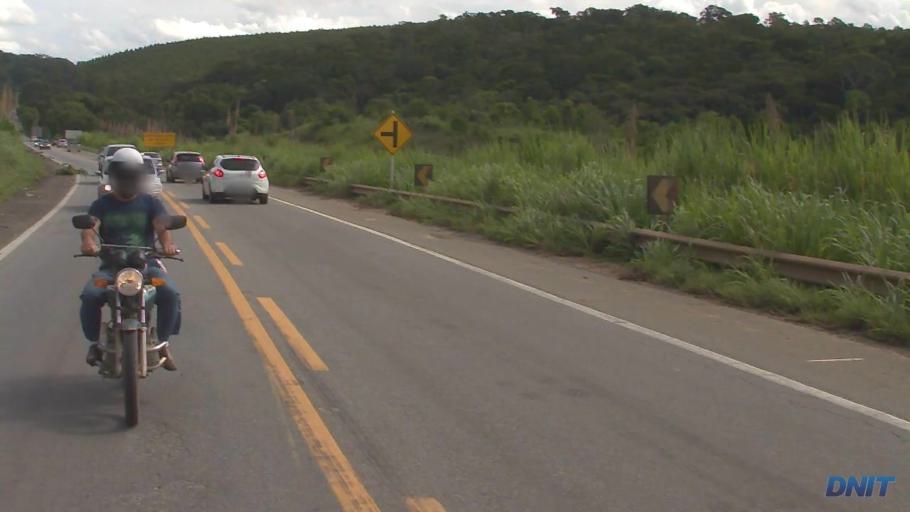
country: BR
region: Minas Gerais
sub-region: Ipaba
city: Ipaba
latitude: -19.3546
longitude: -42.4354
